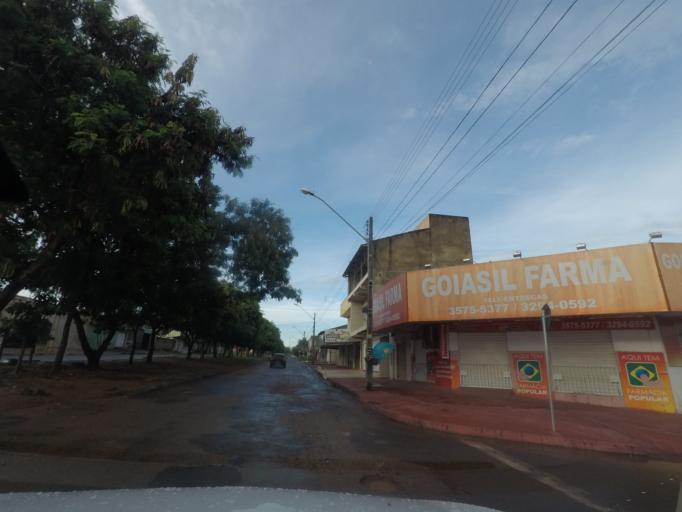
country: BR
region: Goias
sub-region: Goiania
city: Goiania
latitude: -16.7433
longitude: -49.3720
